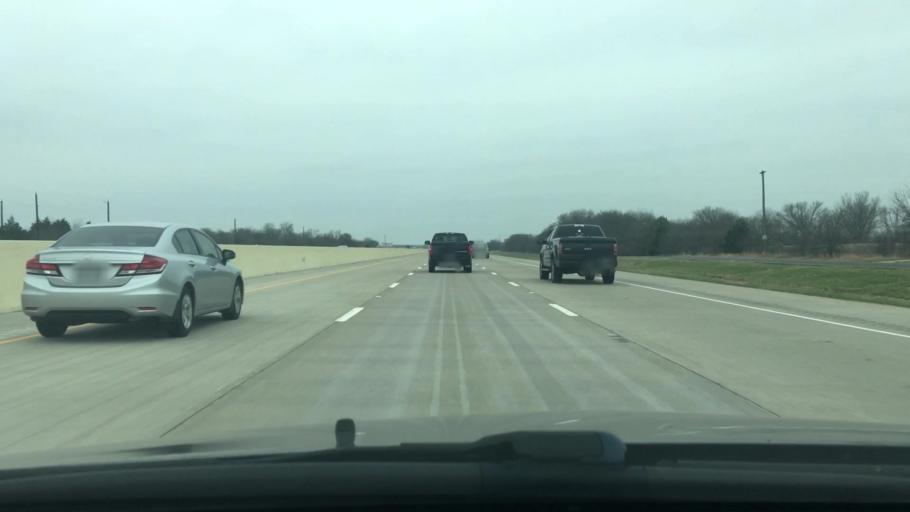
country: US
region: Texas
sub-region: Navarro County
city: Corsicana
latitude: 31.9806
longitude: -96.4237
